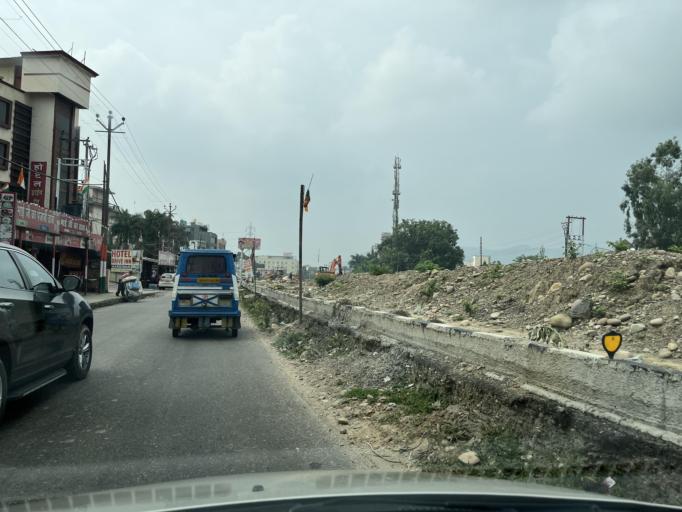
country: IN
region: Uttarakhand
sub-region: Dehradun
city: Raiwala
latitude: 29.9952
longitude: 78.1900
